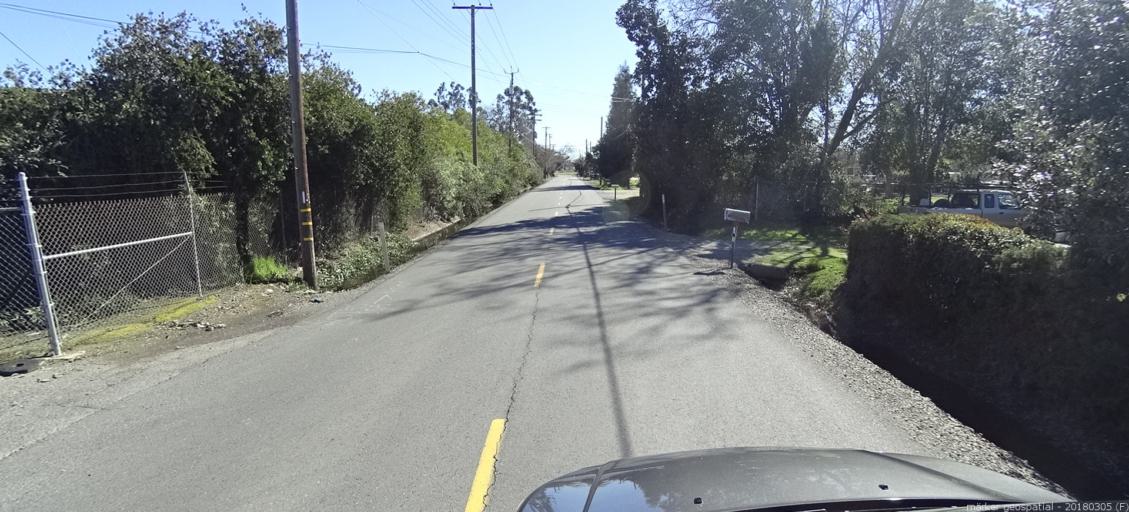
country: US
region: California
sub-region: Sacramento County
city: Florin
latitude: 38.4913
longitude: -121.3974
